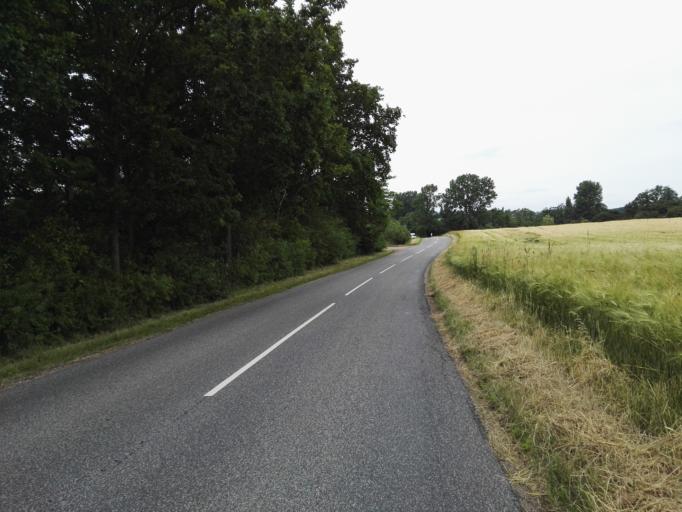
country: DK
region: Capital Region
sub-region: Egedal Kommune
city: Vekso
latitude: 55.7334
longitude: 12.2351
